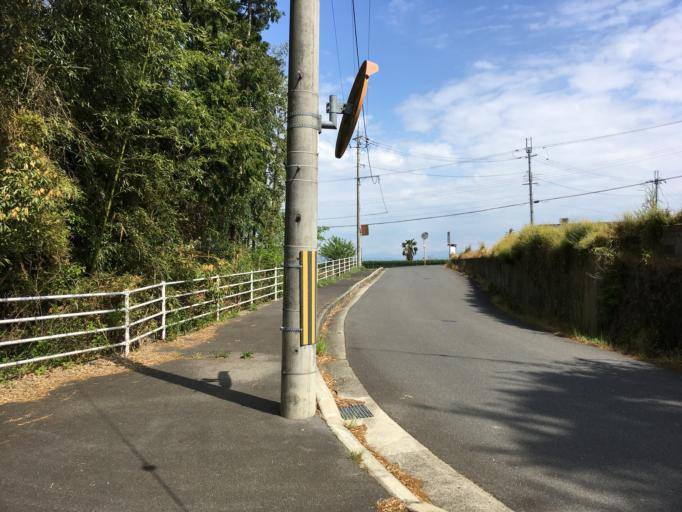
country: JP
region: Nara
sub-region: Ikoma-shi
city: Ikoma
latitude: 34.6297
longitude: 135.6776
